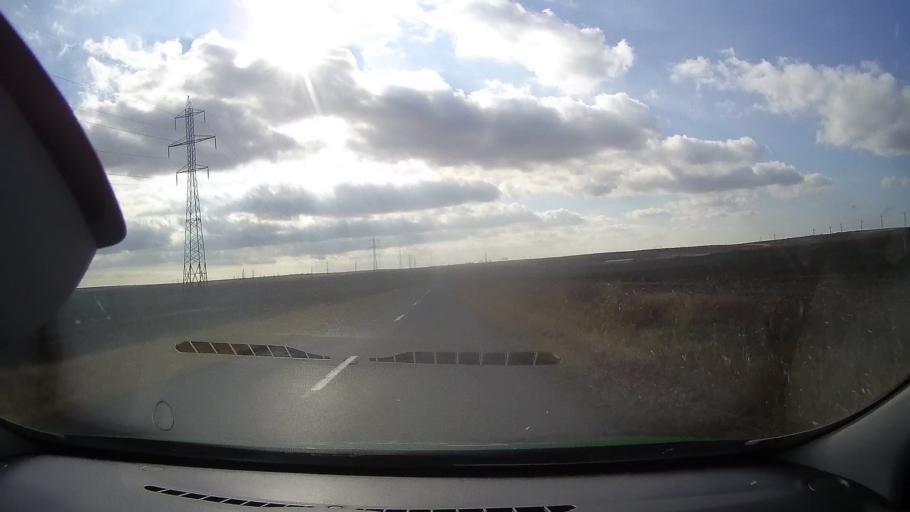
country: RO
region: Constanta
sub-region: Comuna Sacele
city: Sacele
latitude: 44.5004
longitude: 28.6610
